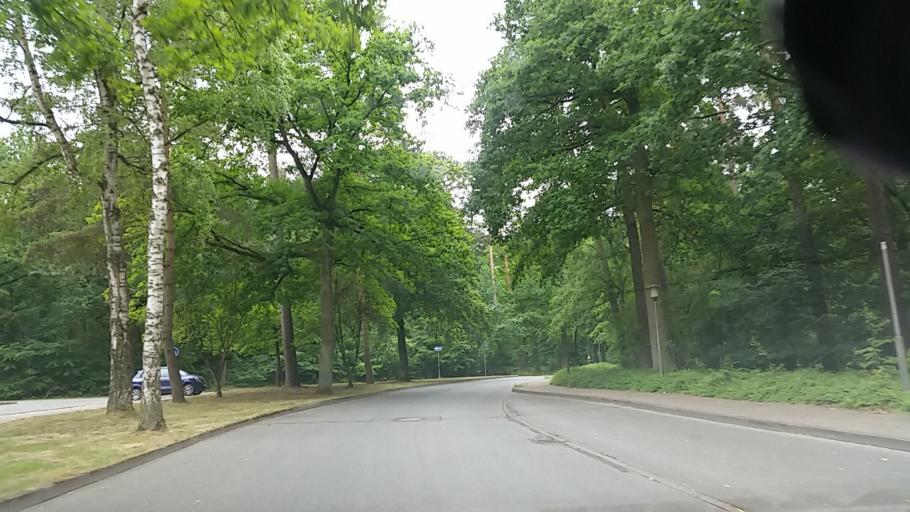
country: DE
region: Lower Saxony
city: Wolfsburg
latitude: 52.4616
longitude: 10.8018
